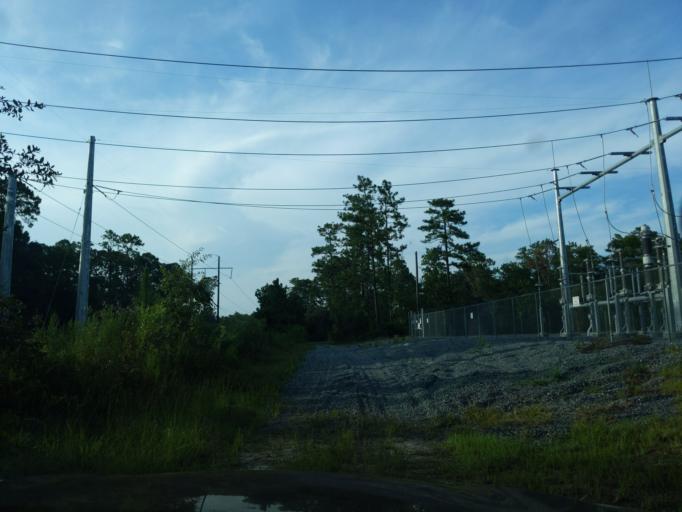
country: US
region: Florida
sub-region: Leon County
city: Tallahassee
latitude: 30.3656
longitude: -84.3611
